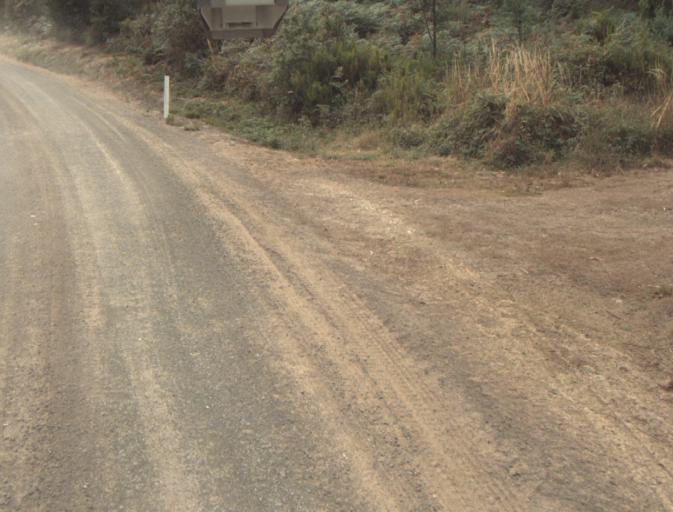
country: AU
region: Tasmania
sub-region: Dorset
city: Bridport
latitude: -41.1774
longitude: 147.2634
